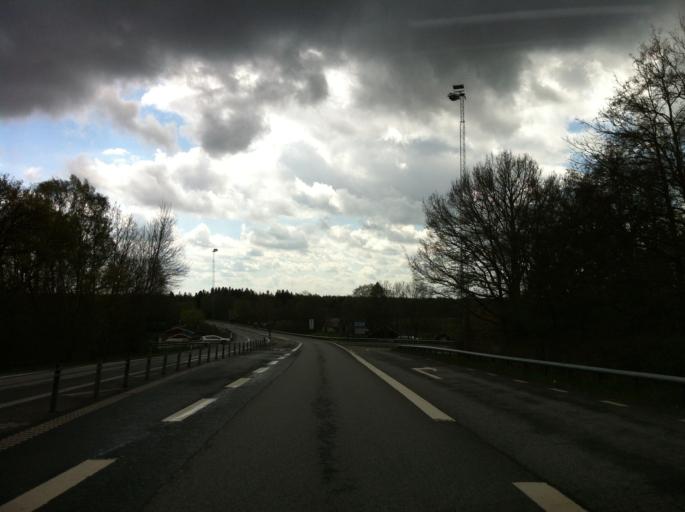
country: SE
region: Skane
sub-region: Hoors Kommun
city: Satofta
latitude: 55.9050
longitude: 13.5215
